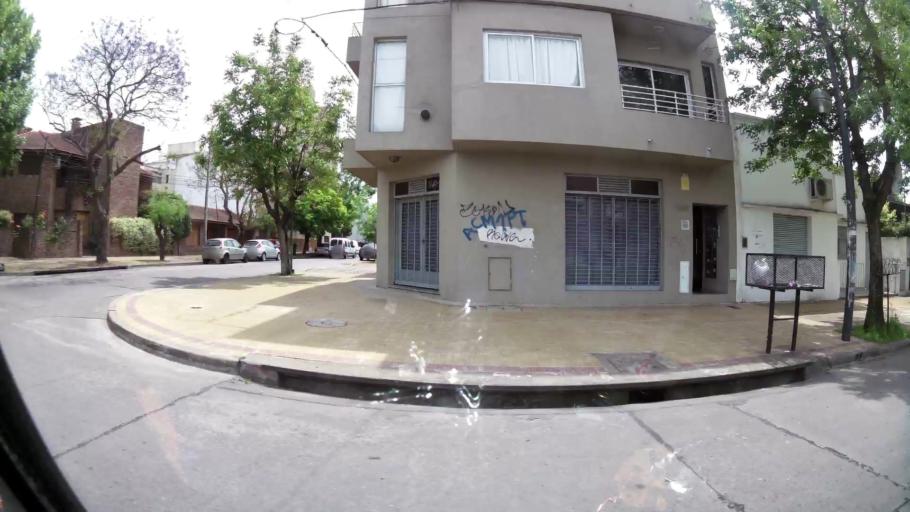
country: AR
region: Buenos Aires
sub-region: Partido de La Plata
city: La Plata
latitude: -34.9455
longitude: -57.9563
